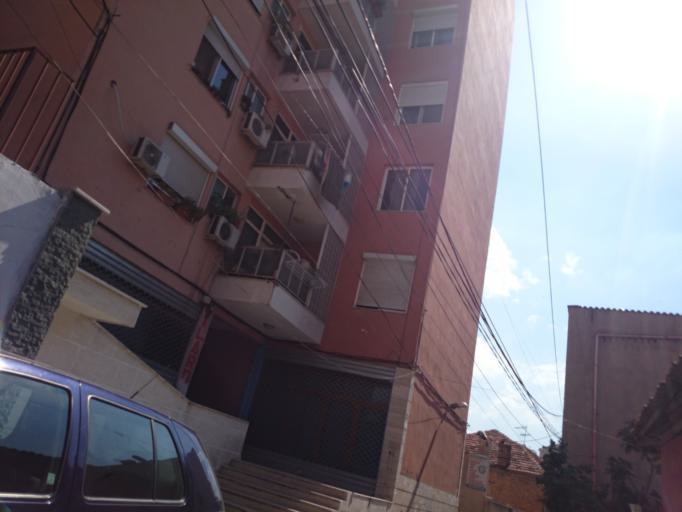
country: AL
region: Tirane
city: Tirana
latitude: 41.3286
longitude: 19.8245
